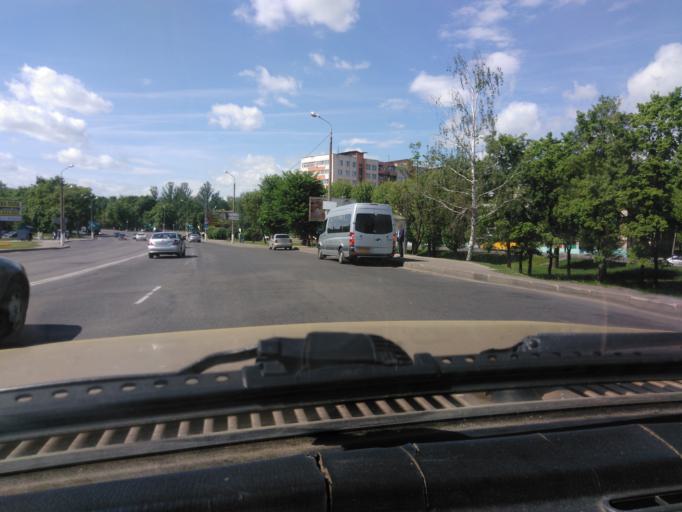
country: BY
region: Mogilev
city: Mahilyow
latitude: 53.9156
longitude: 30.3150
